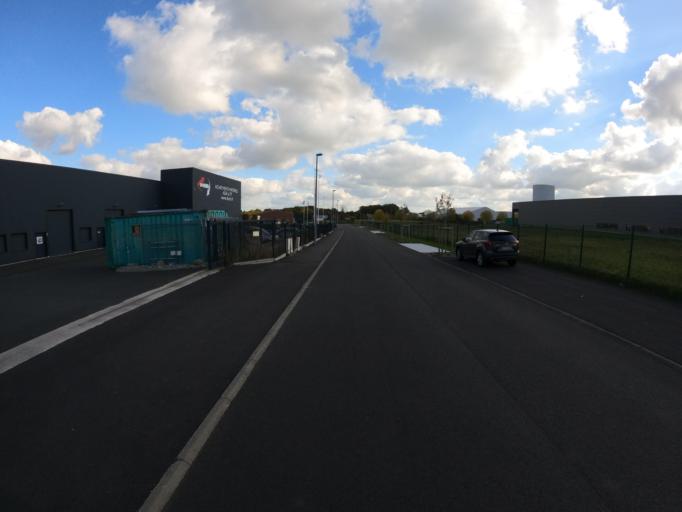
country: FR
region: Pays de la Loire
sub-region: Departement de la Loire-Atlantique
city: Le Bignon
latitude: 47.1008
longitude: -1.4530
